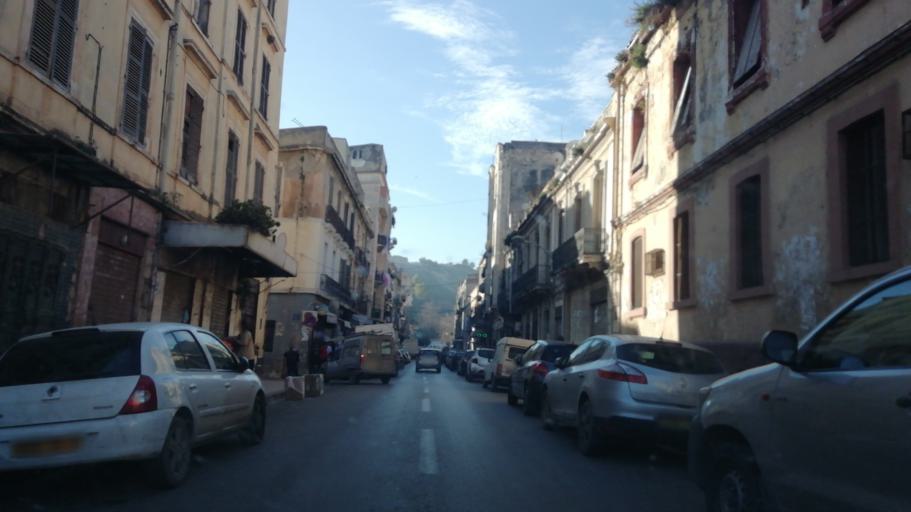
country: DZ
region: Oran
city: Oran
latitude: 35.7037
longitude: -0.6538
